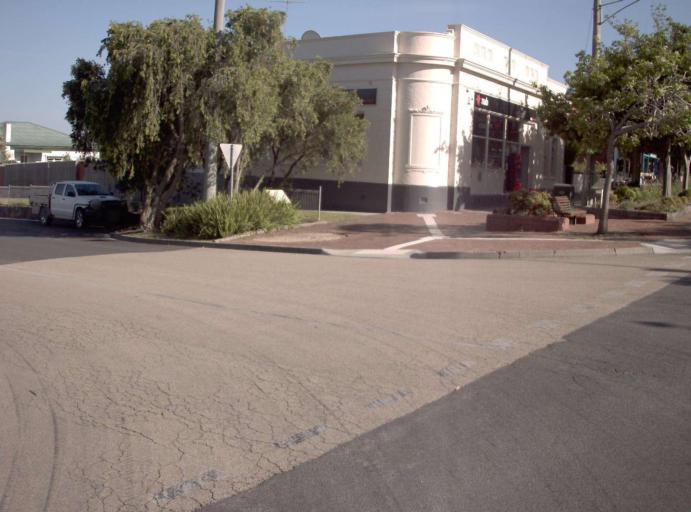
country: AU
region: Victoria
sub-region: East Gippsland
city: Lakes Entrance
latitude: -37.7074
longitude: 148.4548
